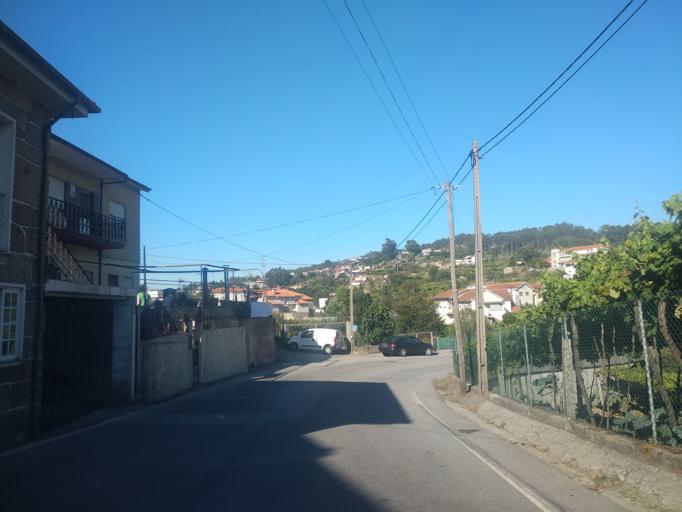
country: PT
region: Porto
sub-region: Penafiel
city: Penafiel
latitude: 41.1999
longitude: -8.2741
